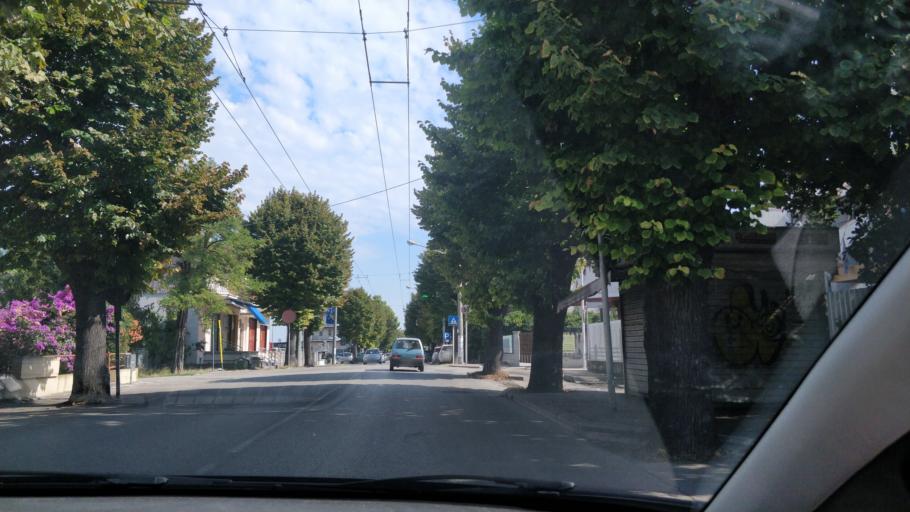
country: IT
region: Abruzzo
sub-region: Provincia di Chieti
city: Chieti
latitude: 42.3763
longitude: 14.1456
